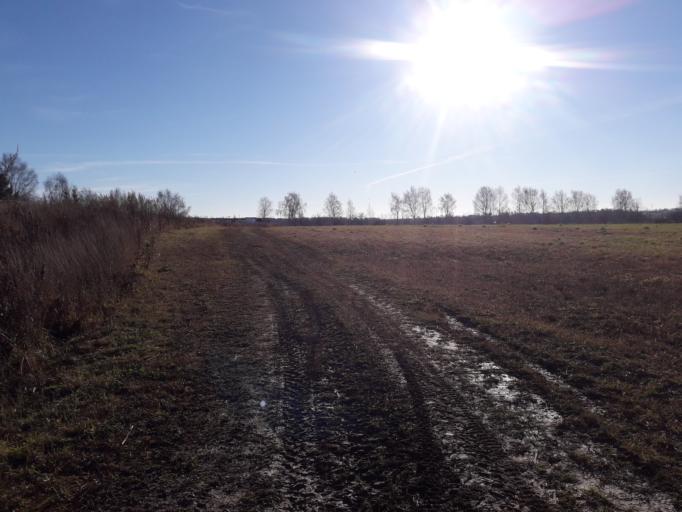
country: RU
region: Moskovskaya
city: Ashukino
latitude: 56.1609
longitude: 37.9681
